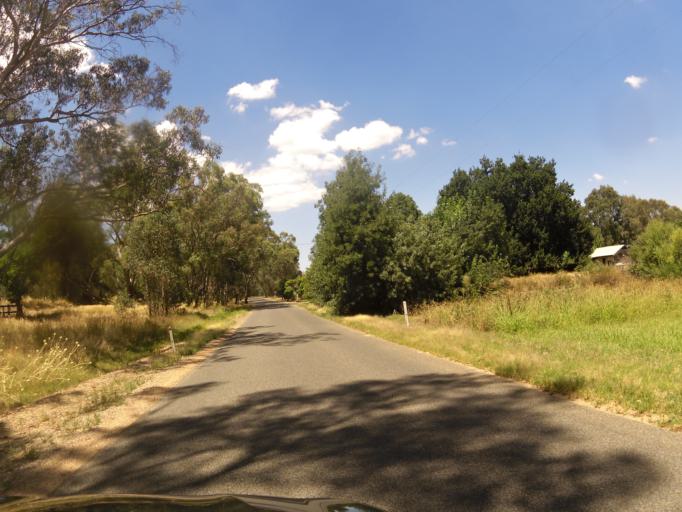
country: AU
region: Victoria
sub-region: Wangaratta
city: Wangaratta
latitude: -36.4055
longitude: 146.5439
